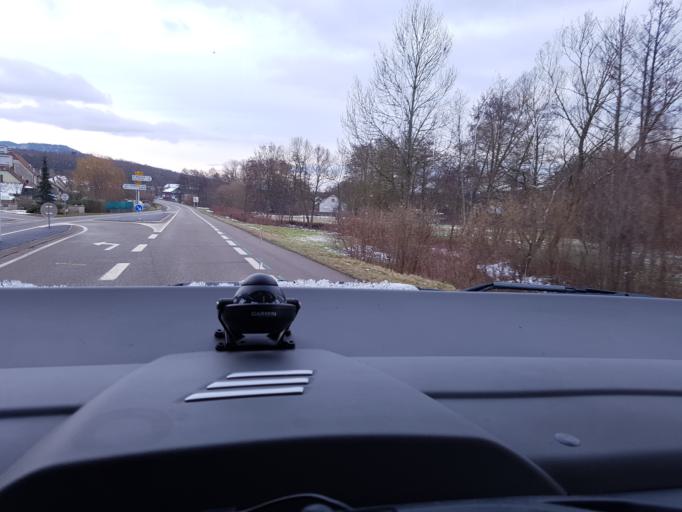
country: FR
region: Alsace
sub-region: Departement du Bas-Rhin
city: Ville
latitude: 48.3387
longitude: 7.3199
